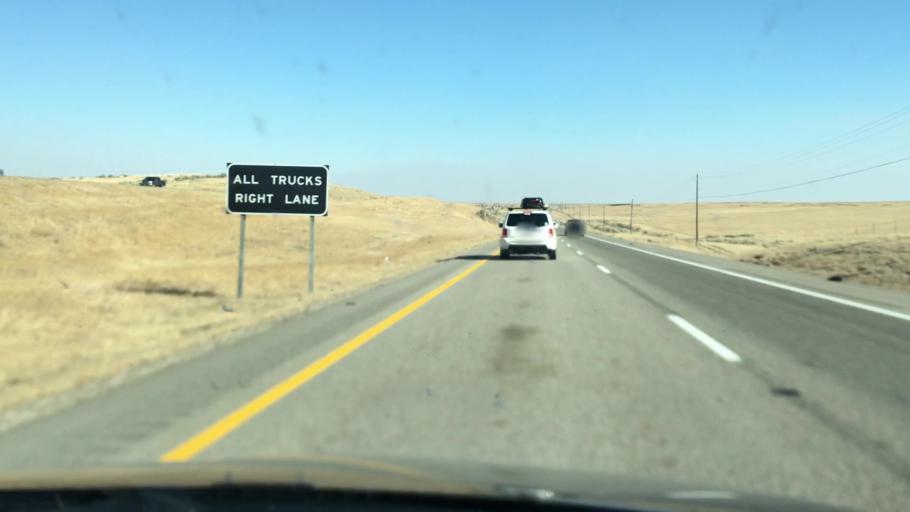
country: US
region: Idaho
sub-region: Ada County
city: Boise
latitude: 43.4483
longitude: -116.0765
